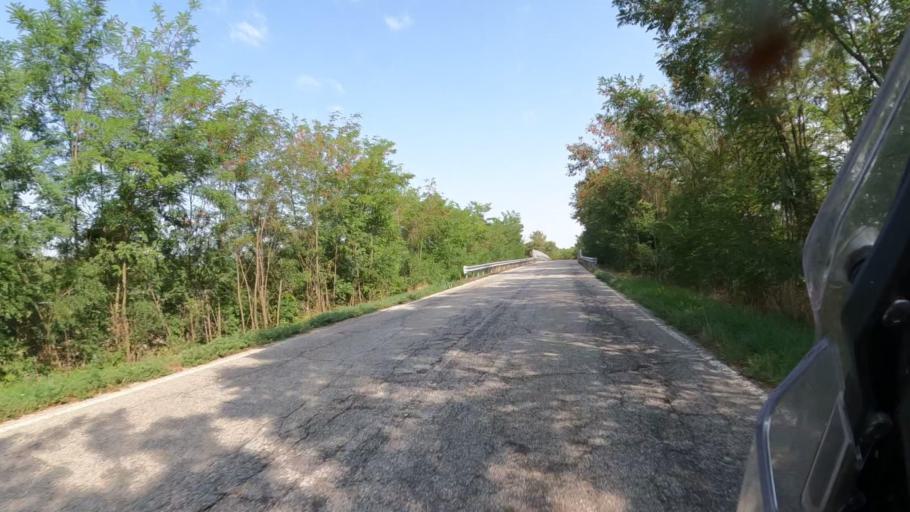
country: IT
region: Piedmont
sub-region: Provincia di Alessandria
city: Quattordio
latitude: 44.9069
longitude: 8.4005
